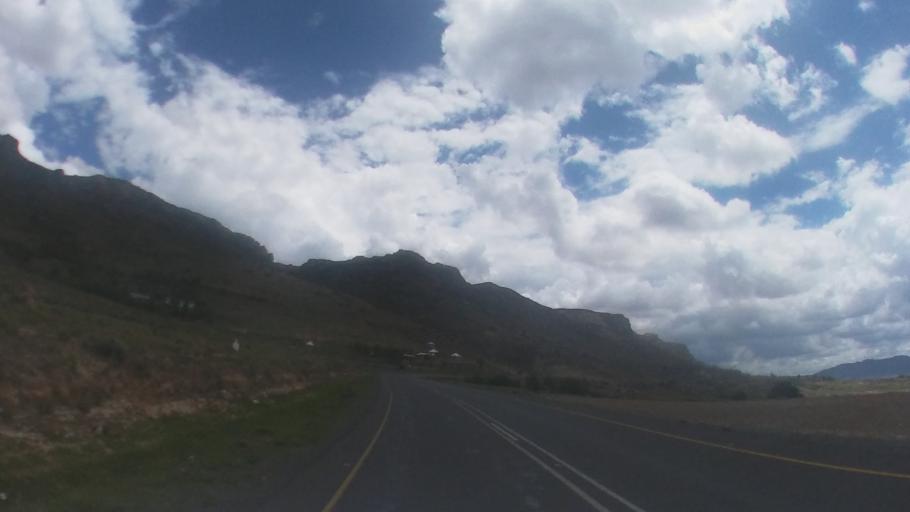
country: LS
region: Maseru
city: Maseru
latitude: -29.4435
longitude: 27.4734
